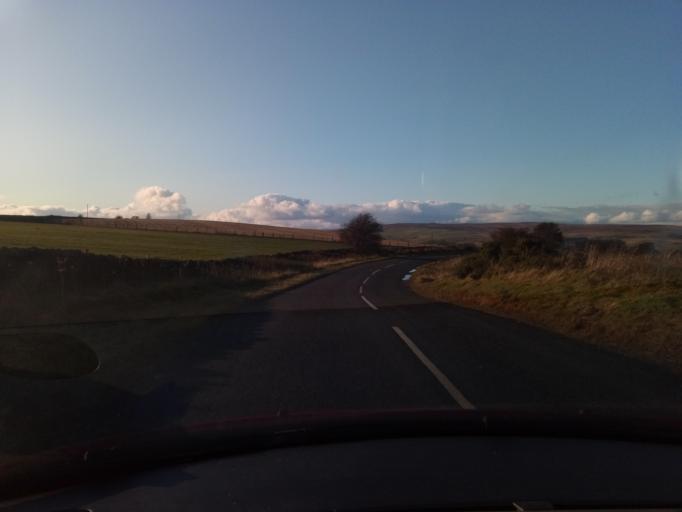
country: GB
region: England
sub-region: County Durham
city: Wolsingham
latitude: 54.7143
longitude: -1.8815
